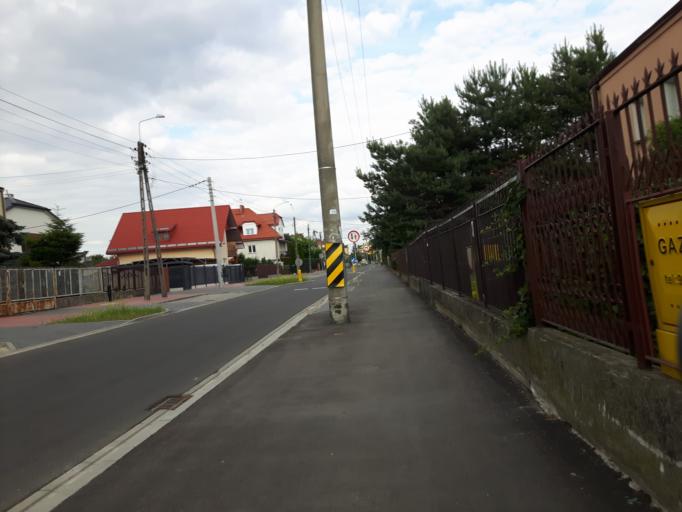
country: PL
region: Masovian Voivodeship
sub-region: Powiat wolominski
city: Zabki
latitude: 52.2872
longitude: 21.1138
